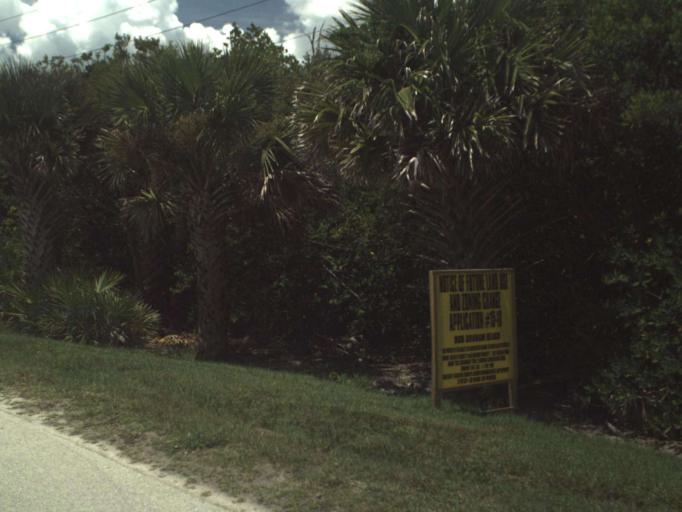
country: US
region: Florida
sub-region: Martin County
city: Sewall's Point
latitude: 27.2393
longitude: -80.1890
